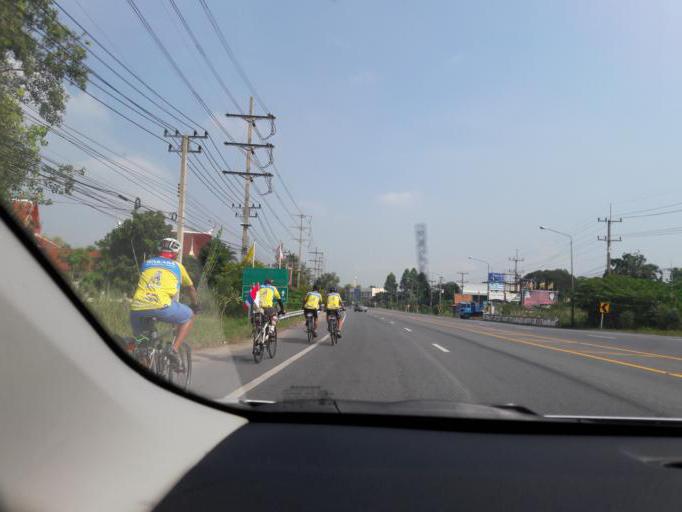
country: TH
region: Ang Thong
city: Ang Thong
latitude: 14.5684
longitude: 100.4532
